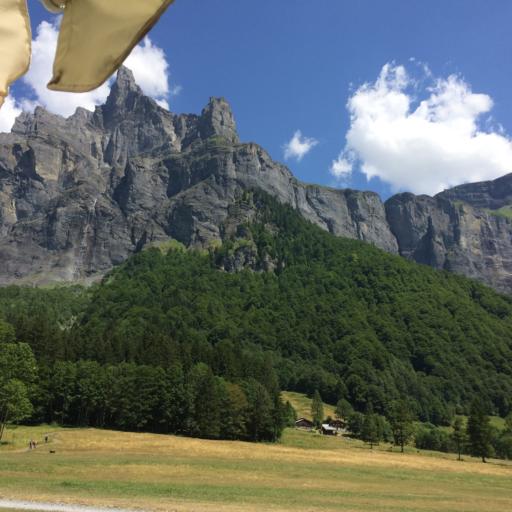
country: CH
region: Valais
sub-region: Monthey District
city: Champery
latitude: 46.0779
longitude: 6.8402
